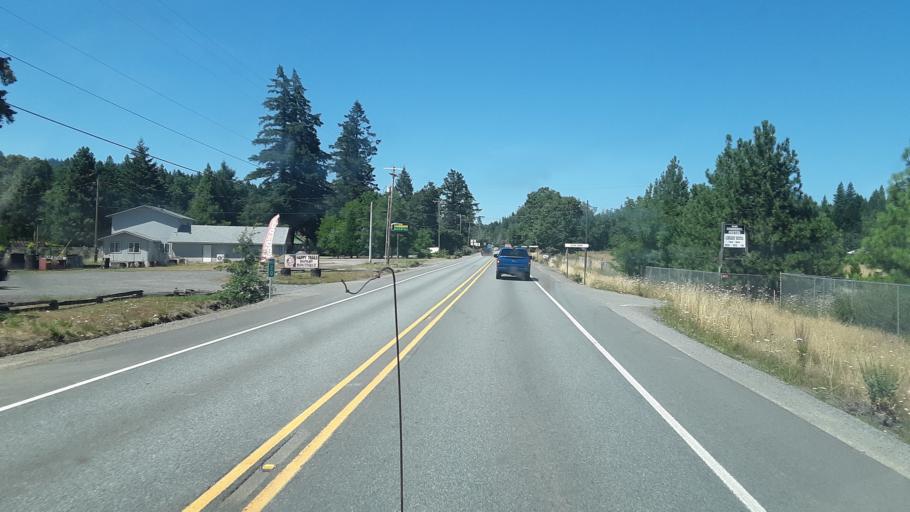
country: US
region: Oregon
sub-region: Josephine County
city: Cave Junction
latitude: 42.2820
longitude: -123.6150
